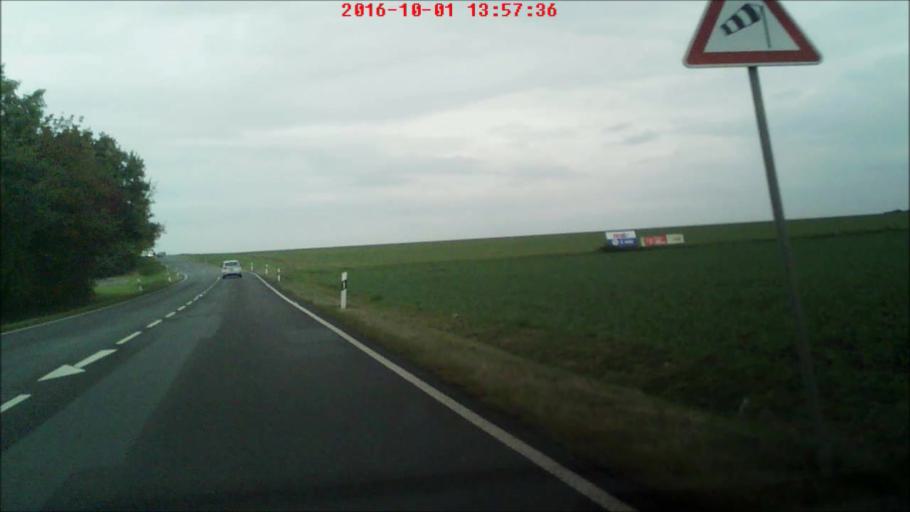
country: DE
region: Thuringia
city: Umpferstedt
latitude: 50.9614
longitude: 11.4079
